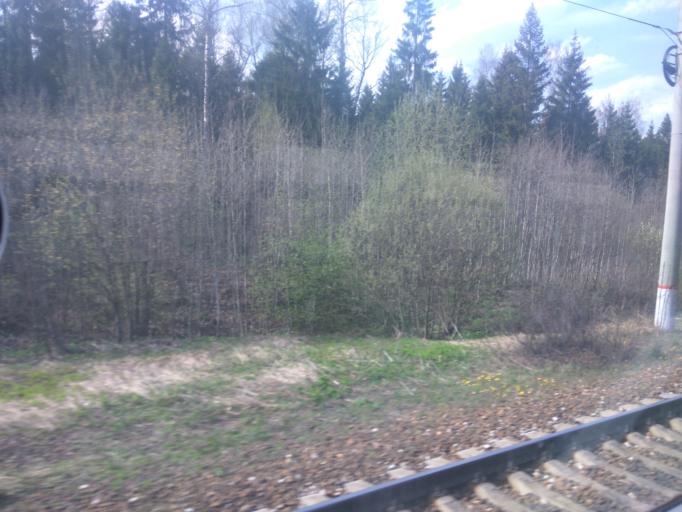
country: RU
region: Moskovskaya
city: Podosinki
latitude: 56.2154
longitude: 37.5269
